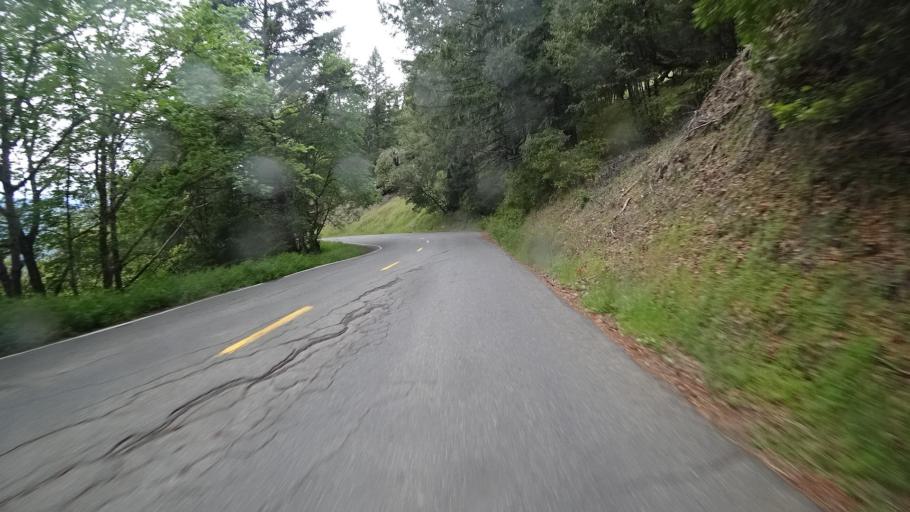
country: US
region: California
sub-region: Humboldt County
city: Redway
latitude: 40.1102
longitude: -123.7673
